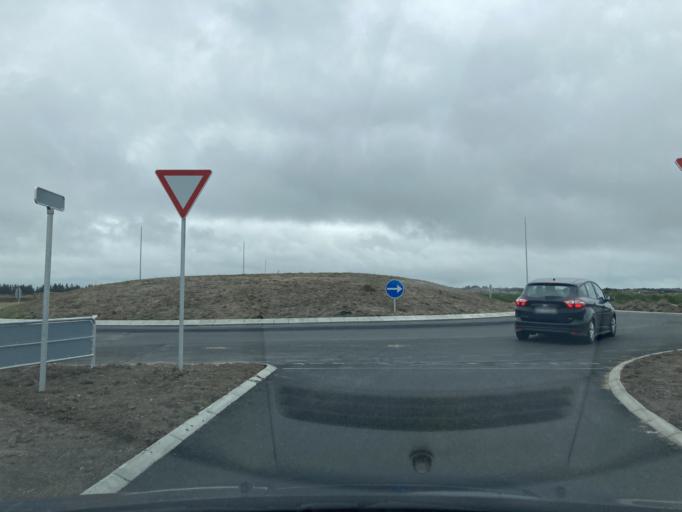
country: DK
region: North Denmark
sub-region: Thisted Kommune
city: Hurup
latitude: 56.9455
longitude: 8.3873
